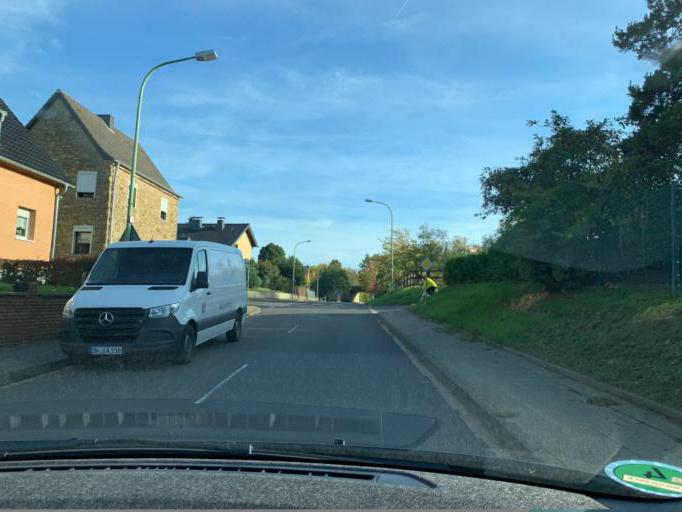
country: DE
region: North Rhine-Westphalia
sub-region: Regierungsbezirk Koln
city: Nideggen
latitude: 50.7040
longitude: 6.5213
